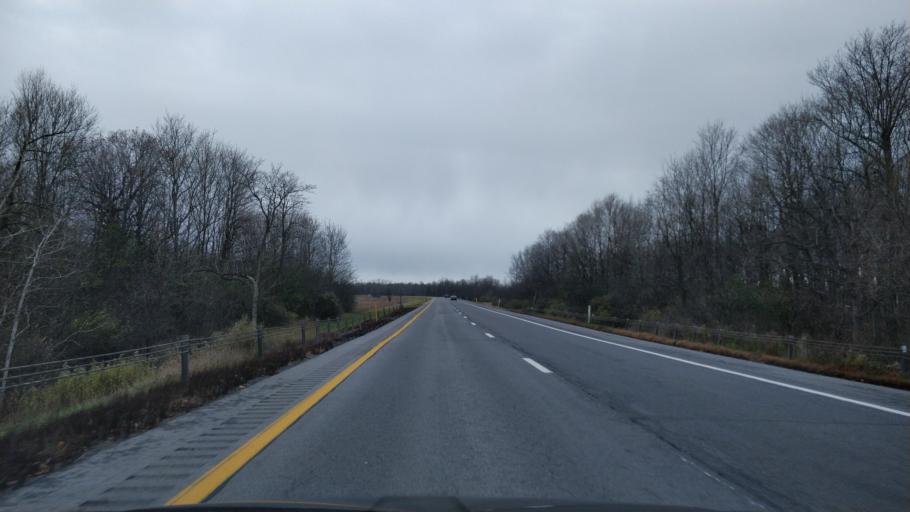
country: US
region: New York
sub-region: Jefferson County
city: Calcium
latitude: 44.1027
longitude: -75.9042
